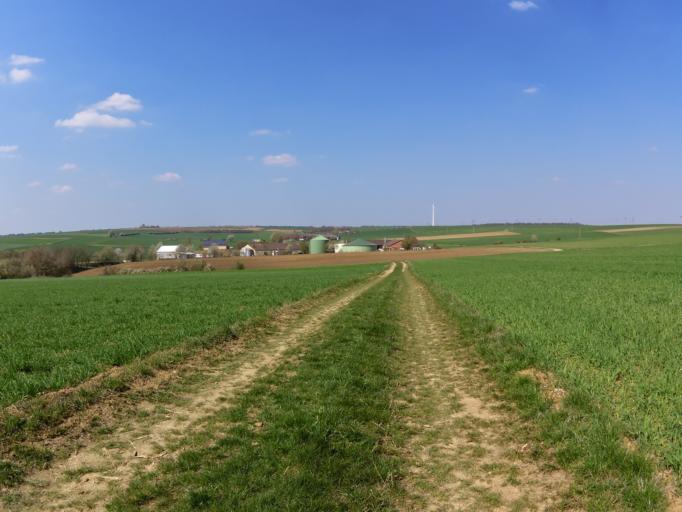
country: DE
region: Bavaria
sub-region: Regierungsbezirk Unterfranken
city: Theilheim
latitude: 49.7585
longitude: 10.0409
